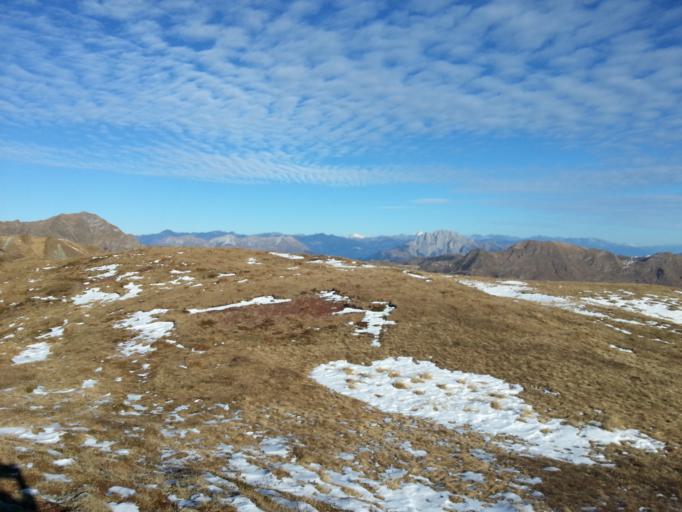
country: IT
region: Friuli Venezia Giulia
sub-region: Provincia di Udine
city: Ligosullo
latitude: 46.5628
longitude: 13.0719
